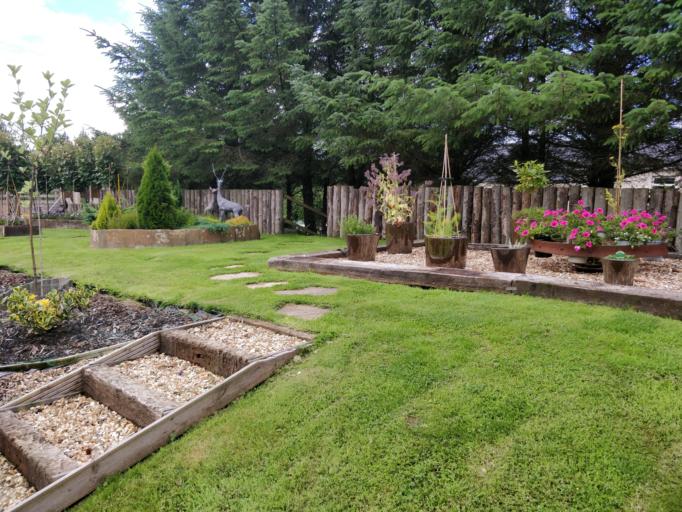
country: GB
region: Scotland
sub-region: Highland
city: Thurso
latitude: 58.4679
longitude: -3.4277
